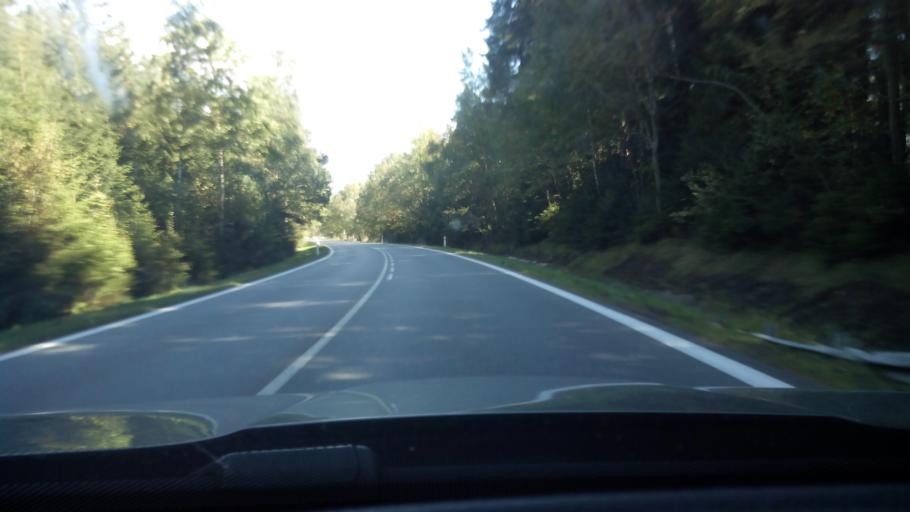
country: CZ
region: Jihocesky
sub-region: Okres Prachatice
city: Vimperk
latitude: 49.0625
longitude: 13.7416
